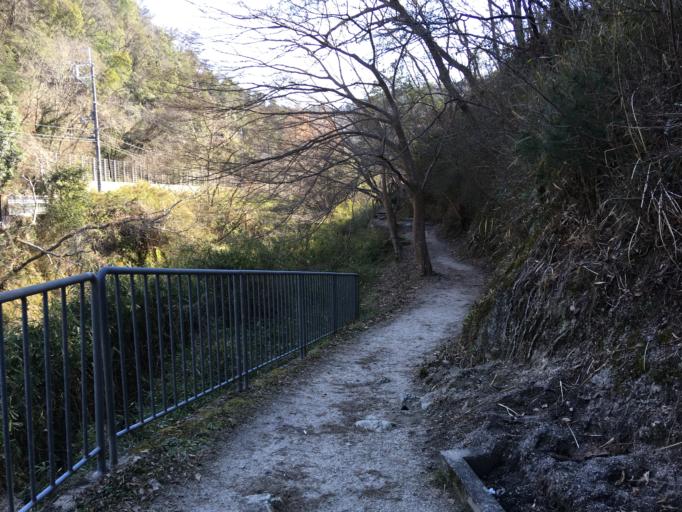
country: JP
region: Osaka
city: Neyagawa
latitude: 34.7572
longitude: 135.6904
